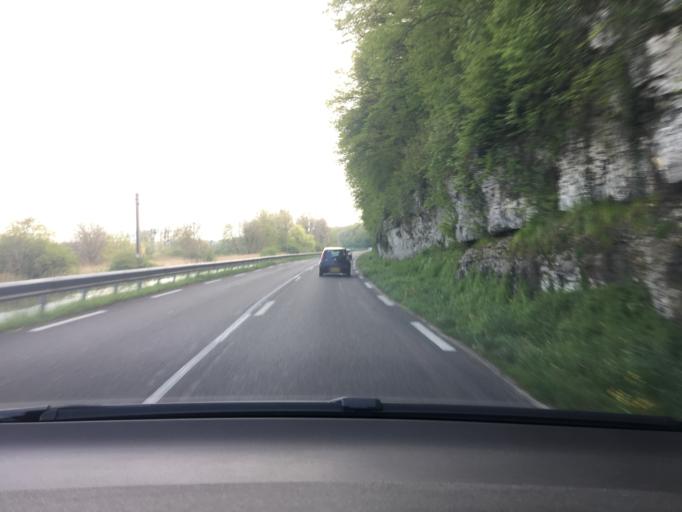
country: FR
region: Franche-Comte
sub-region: Departement du Doubs
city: Bart
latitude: 47.4850
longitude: 6.7719
